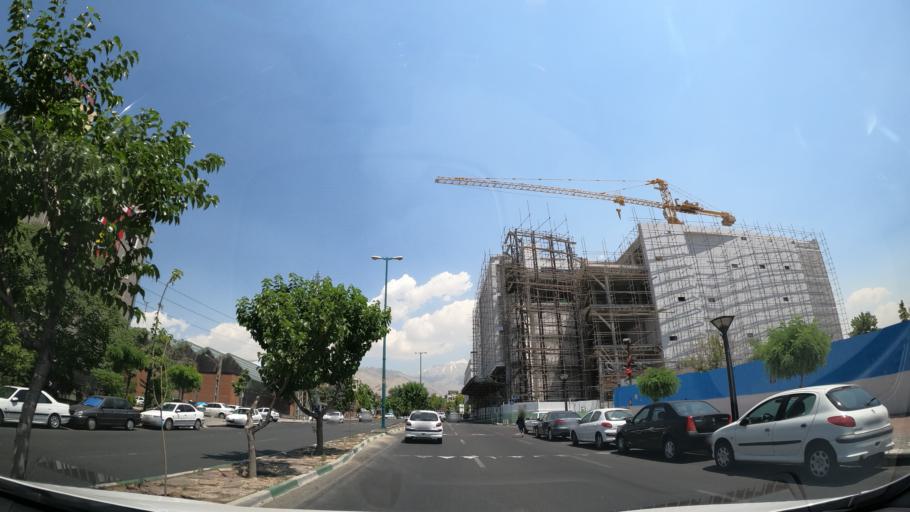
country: IR
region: Tehran
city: Tajrish
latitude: 35.7693
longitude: 51.3789
